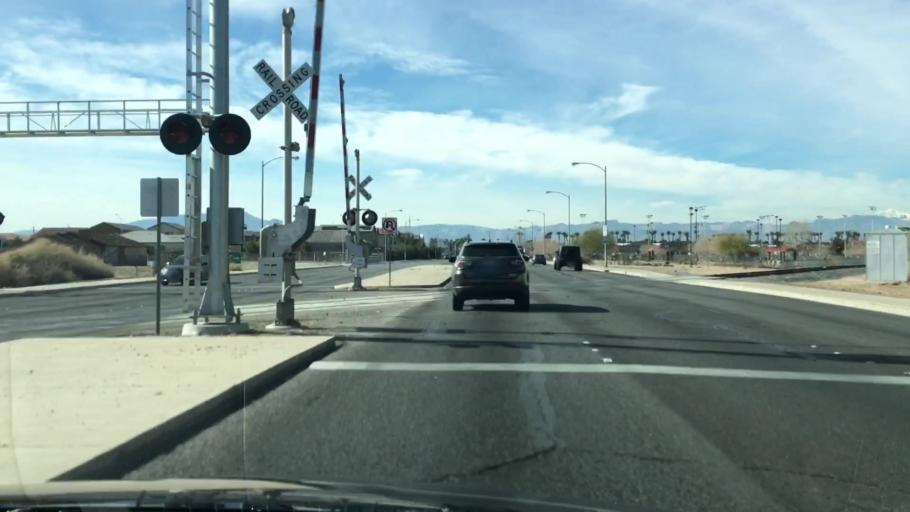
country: US
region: Nevada
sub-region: Clark County
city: Whitney
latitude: 36.0570
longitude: -115.1119
